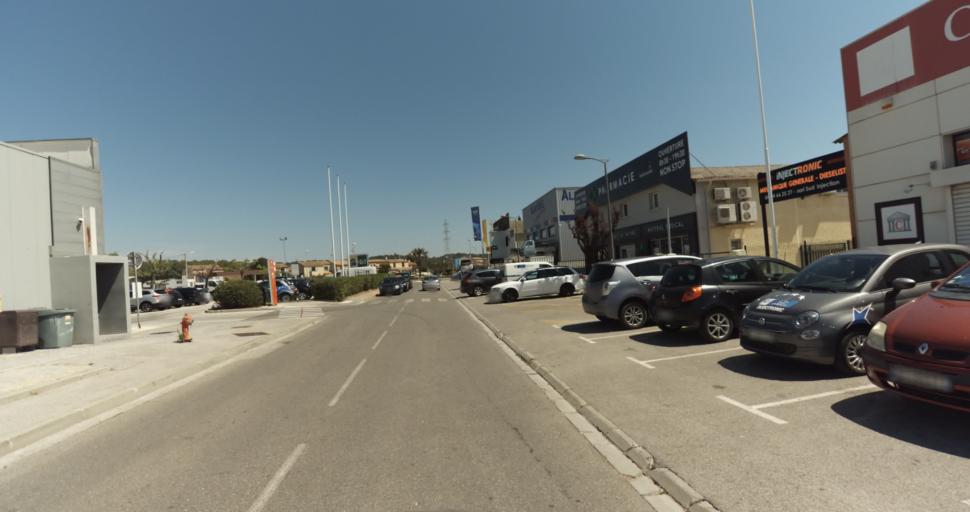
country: FR
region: Provence-Alpes-Cote d'Azur
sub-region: Departement du Var
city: La Crau
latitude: 43.1532
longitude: 6.0696
